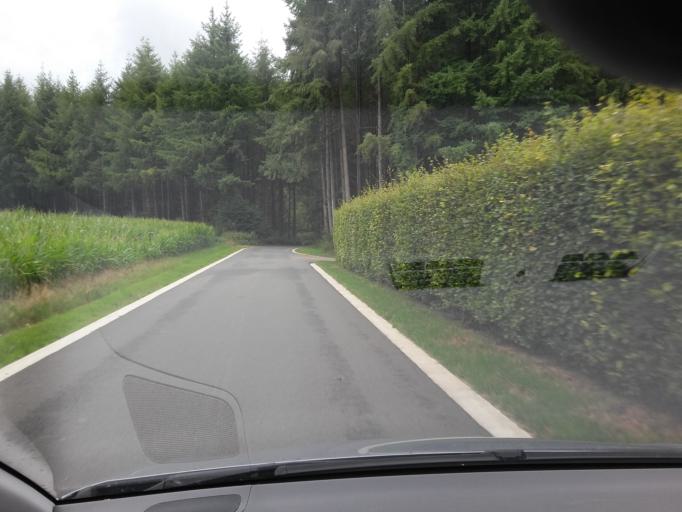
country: BE
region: Wallonia
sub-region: Province du Luxembourg
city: Arlon
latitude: 49.7190
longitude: 5.8331
